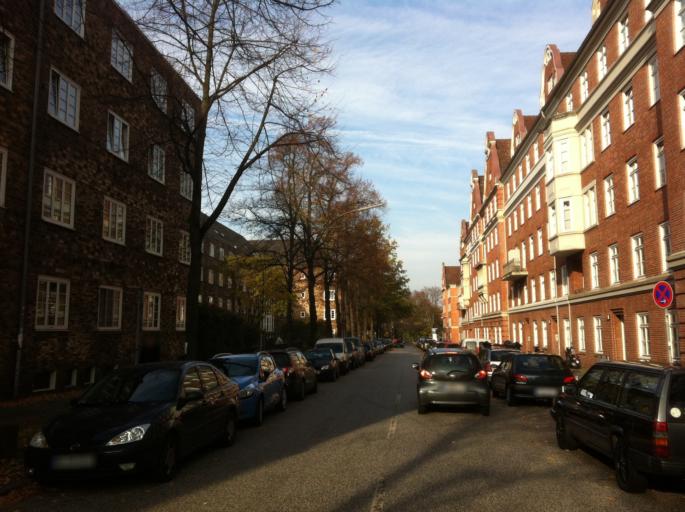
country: DE
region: Hamburg
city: Altona
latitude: 53.5636
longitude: 9.9294
